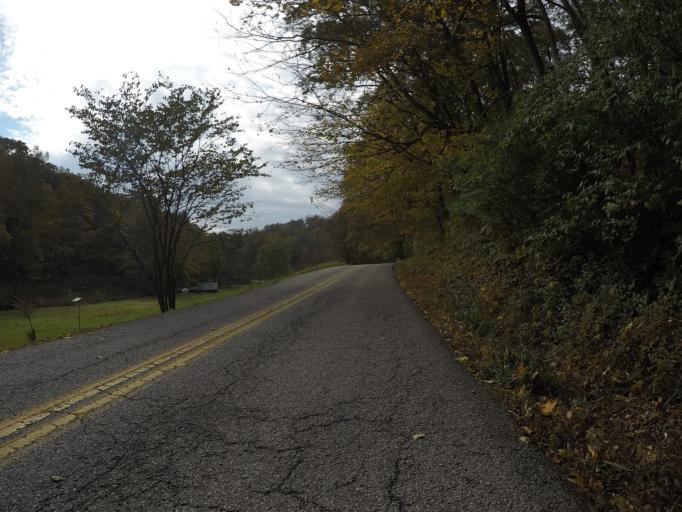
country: US
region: West Virginia
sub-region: Cabell County
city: Huntington
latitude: 38.3765
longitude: -82.4053
